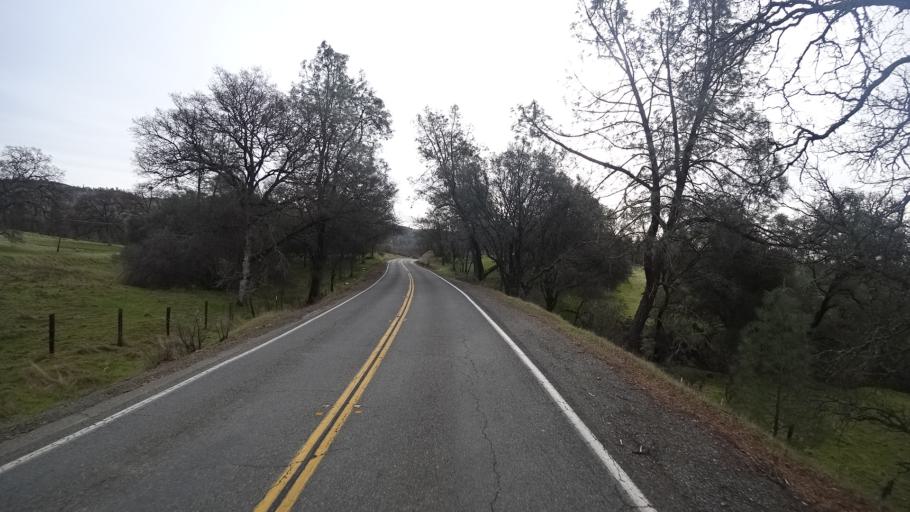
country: US
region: California
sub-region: Butte County
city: Oroville East
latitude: 39.4461
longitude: -121.4365
